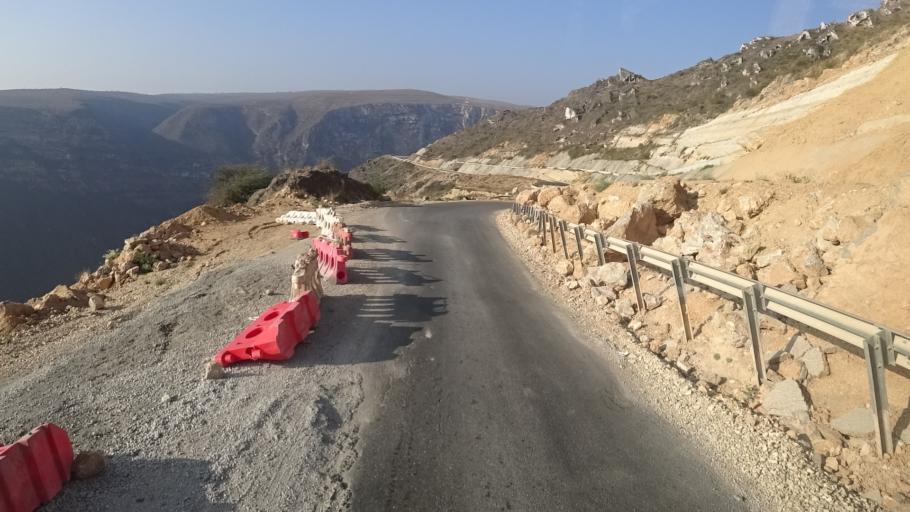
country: YE
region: Al Mahrah
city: Hawf
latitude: 16.7560
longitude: 53.2217
